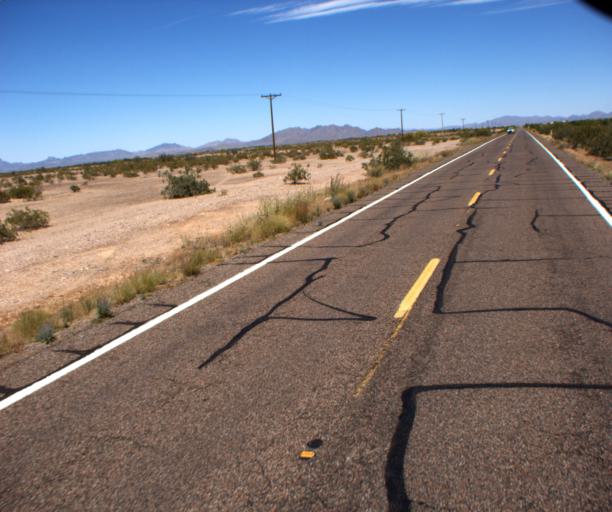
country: US
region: Arizona
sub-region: Maricopa County
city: Gila Bend
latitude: 32.8887
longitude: -112.7497
